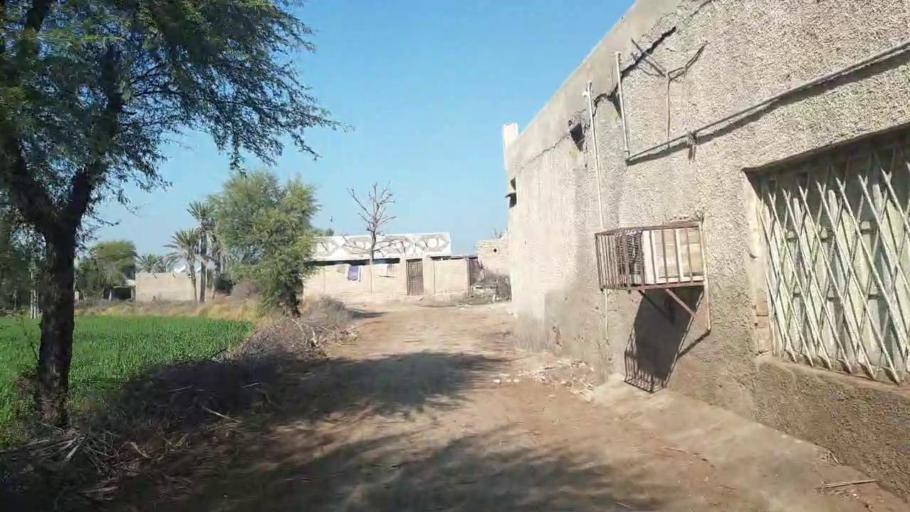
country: PK
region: Sindh
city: Shahdadpur
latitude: 25.9109
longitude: 68.5550
